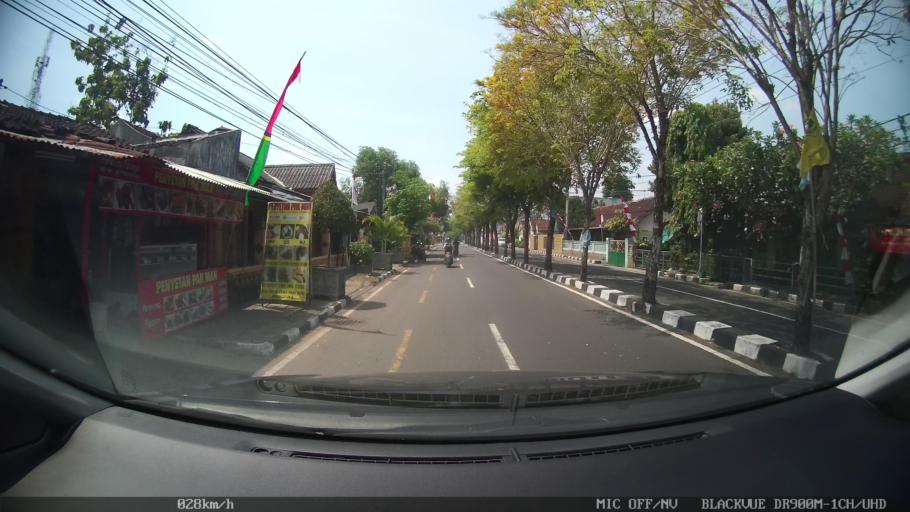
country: ID
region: Daerah Istimewa Yogyakarta
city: Yogyakarta
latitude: -7.8194
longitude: 110.3962
